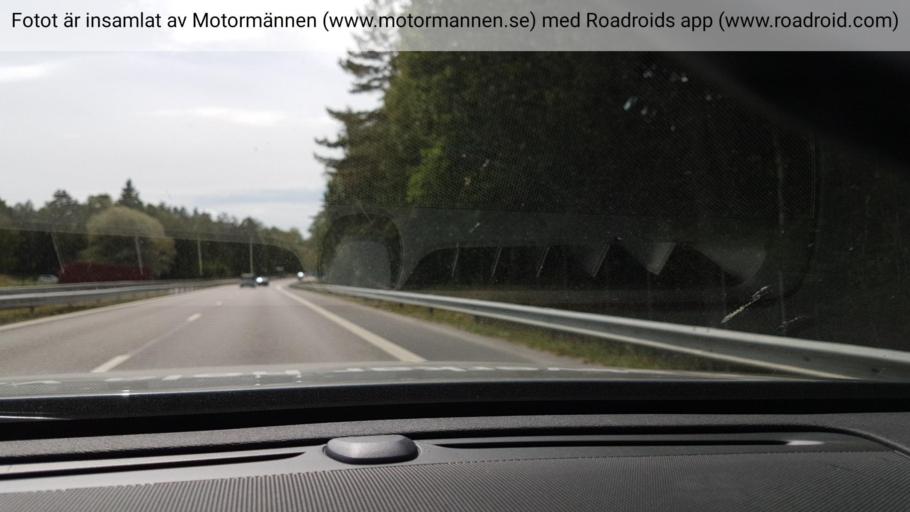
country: SE
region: Vaestra Goetaland
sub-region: Alingsas Kommun
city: Ingared
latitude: 57.8754
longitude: 12.4928
